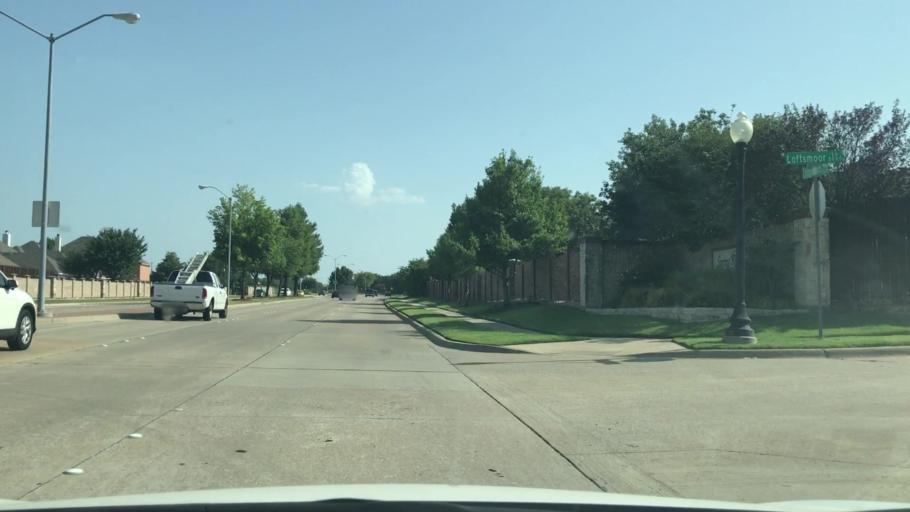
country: US
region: Texas
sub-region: Collin County
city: Allen
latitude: 33.0911
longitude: -96.7492
